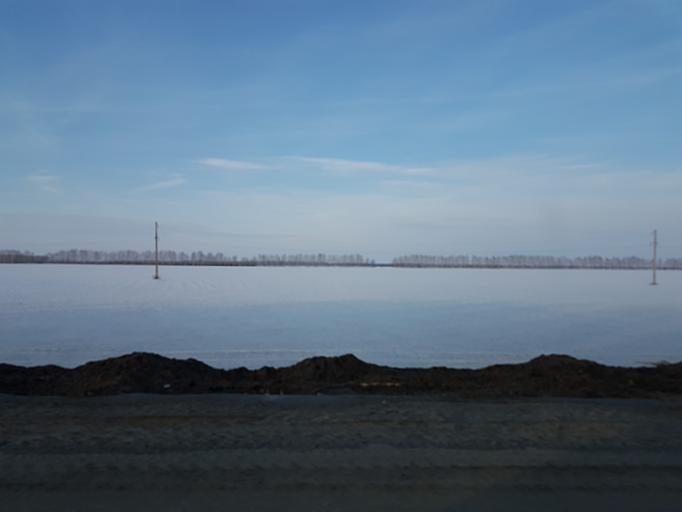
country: RU
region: Tambov
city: Zavoronezhskoye
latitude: 52.8333
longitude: 40.8767
